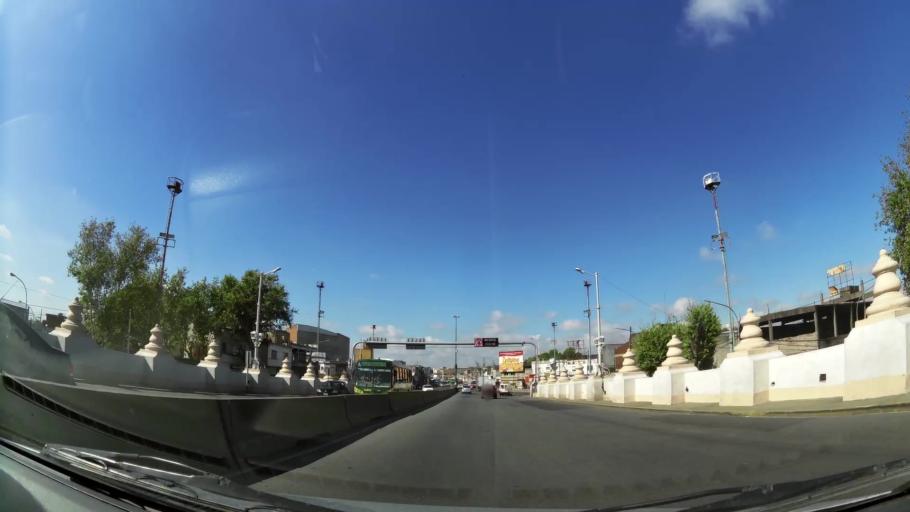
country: AR
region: Buenos Aires
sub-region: Partido de Lanus
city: Lanus
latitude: -34.6616
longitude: -58.4170
